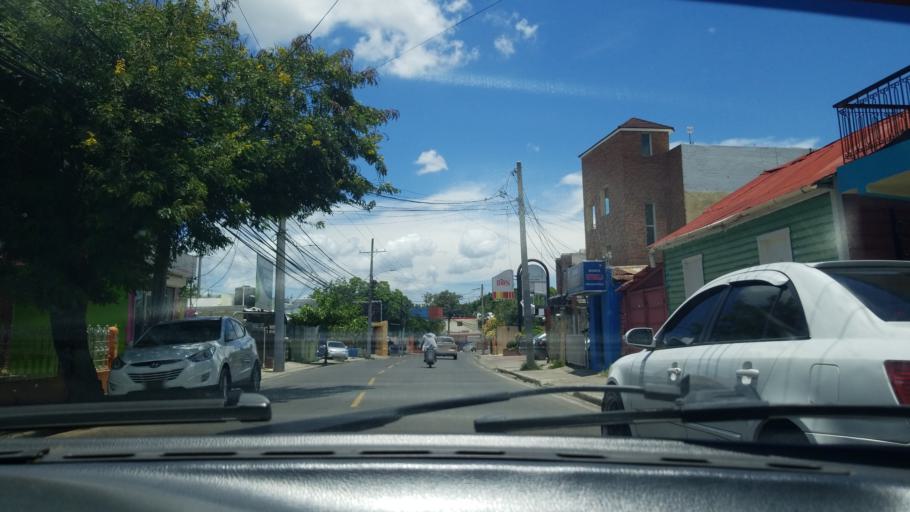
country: DO
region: Santiago
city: Santiago de los Caballeros
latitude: 19.4757
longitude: -70.6856
